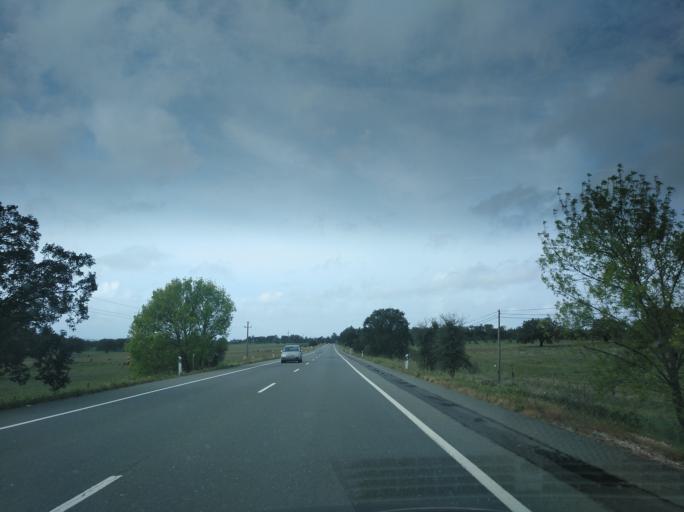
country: PT
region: Setubal
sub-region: Grandola
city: Grandola
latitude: 38.1499
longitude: -8.5119
